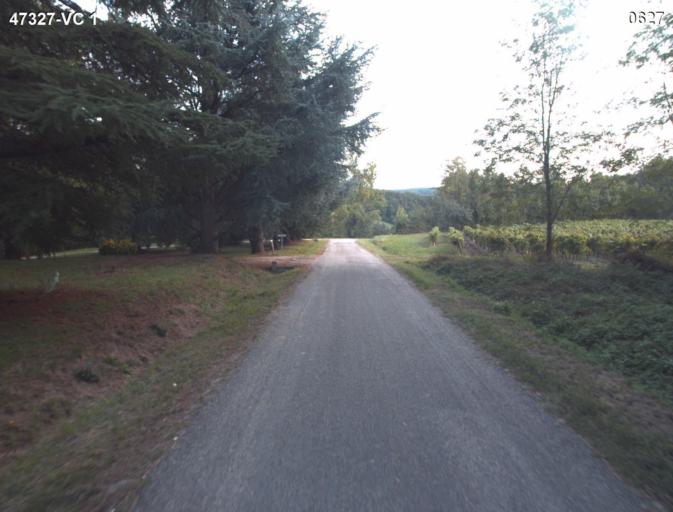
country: FR
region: Aquitaine
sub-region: Departement du Lot-et-Garonne
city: Barbaste
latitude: 44.1905
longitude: 0.2556
